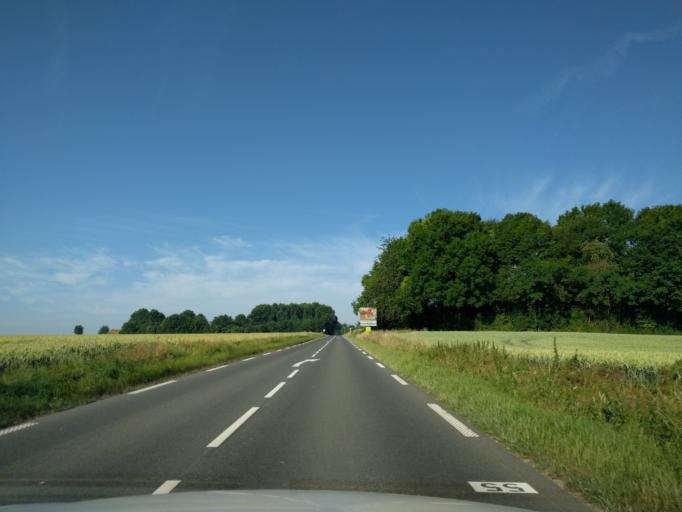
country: FR
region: Picardie
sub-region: Departement de l'Oise
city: Maignelay-Montigny
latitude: 49.6332
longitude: 2.4650
